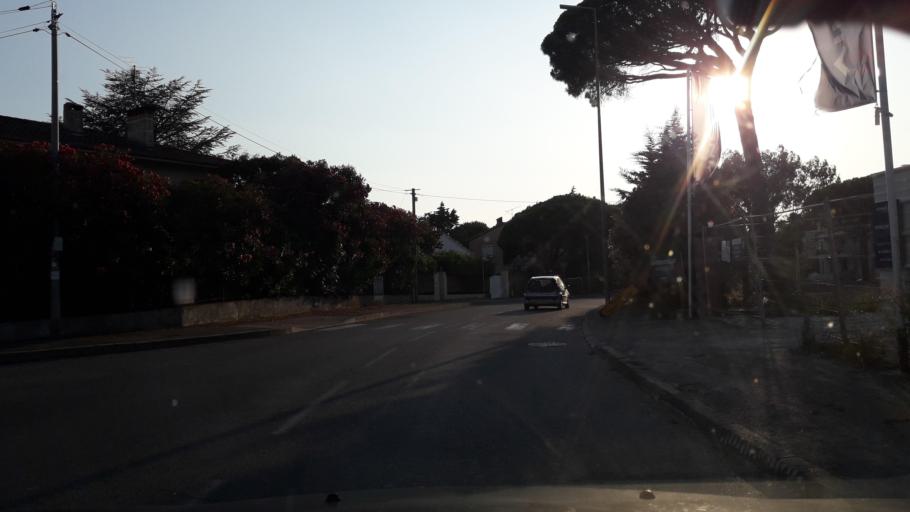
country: FR
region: Provence-Alpes-Cote d'Azur
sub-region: Departement du Var
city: Saint-Raphael
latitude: 43.4367
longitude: 6.7714
